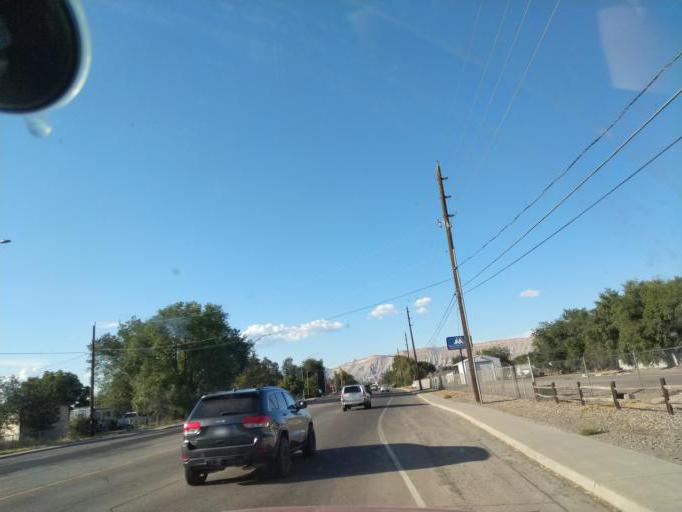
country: US
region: Colorado
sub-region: Mesa County
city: Clifton
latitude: 39.0710
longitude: -108.4593
